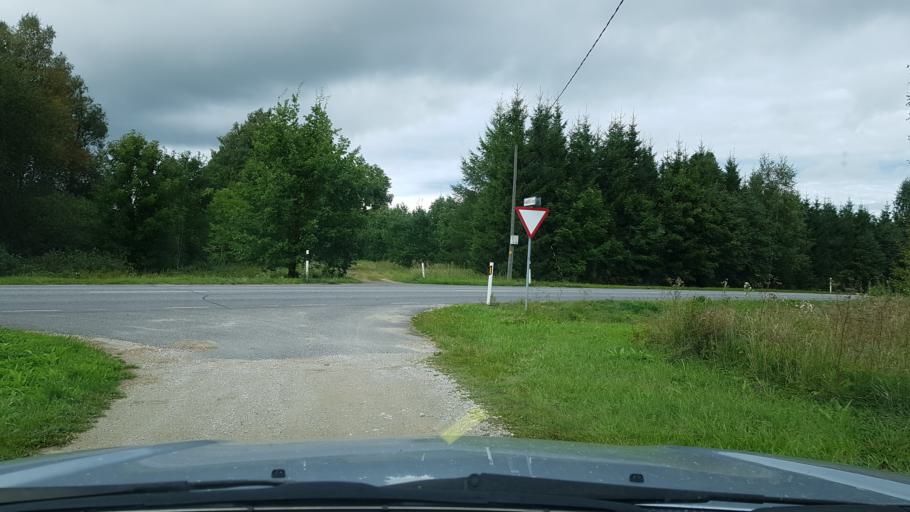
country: EE
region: Harju
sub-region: Raasiku vald
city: Arukula
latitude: 59.3612
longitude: 25.0052
